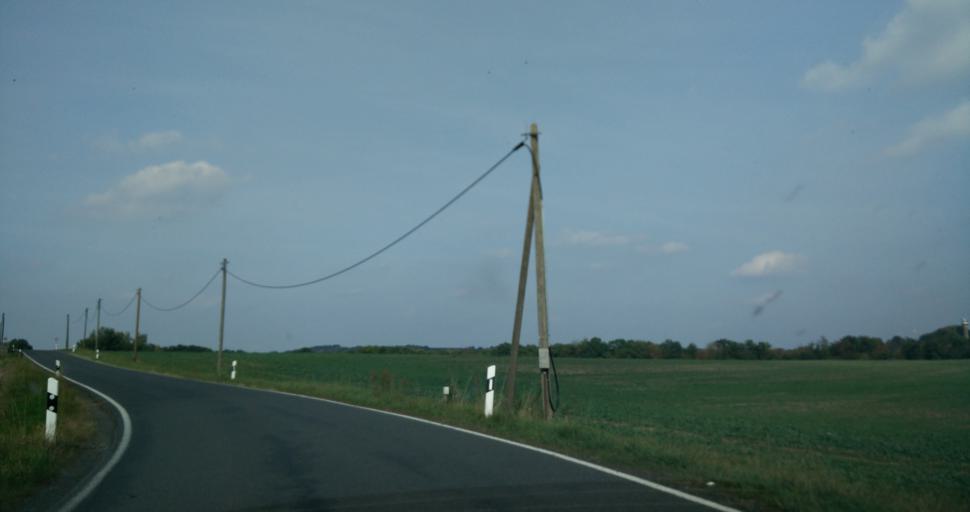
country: DE
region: Saxony
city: Colditz
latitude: 51.1144
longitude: 12.8024
